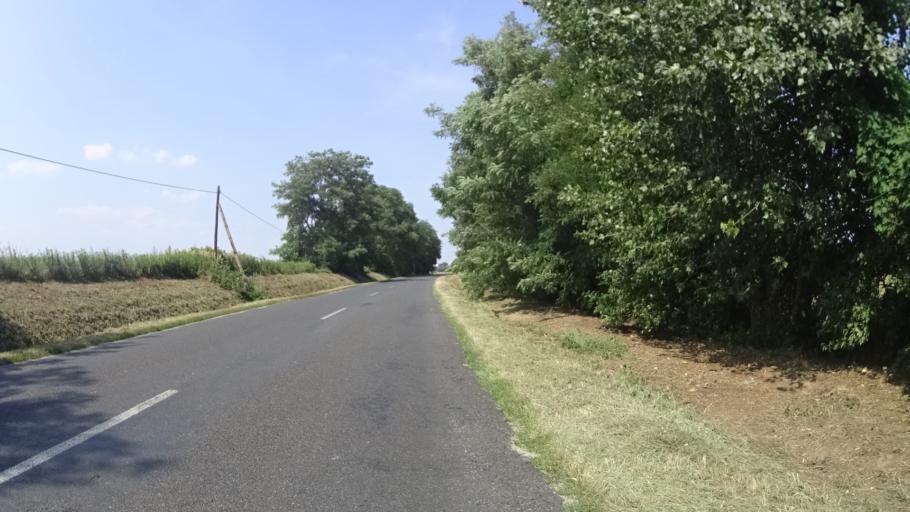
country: HU
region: Zala
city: Nagykanizsa
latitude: 46.4309
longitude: 16.9533
